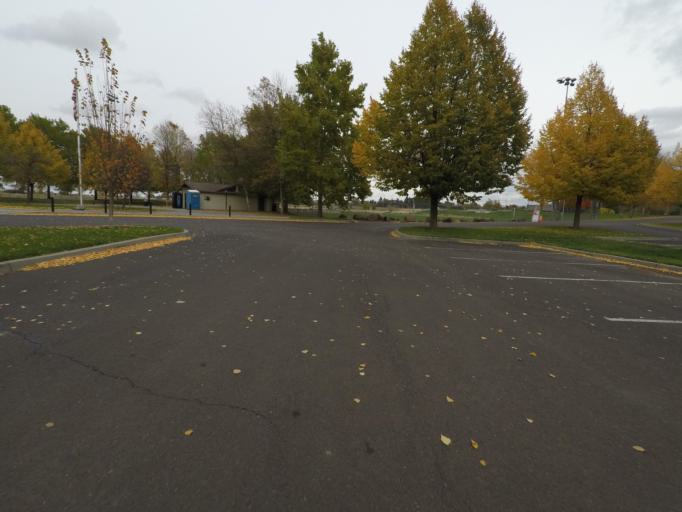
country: US
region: Washington
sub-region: Walla Walla County
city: Walla Walla East
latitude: 46.0726
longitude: -118.2894
